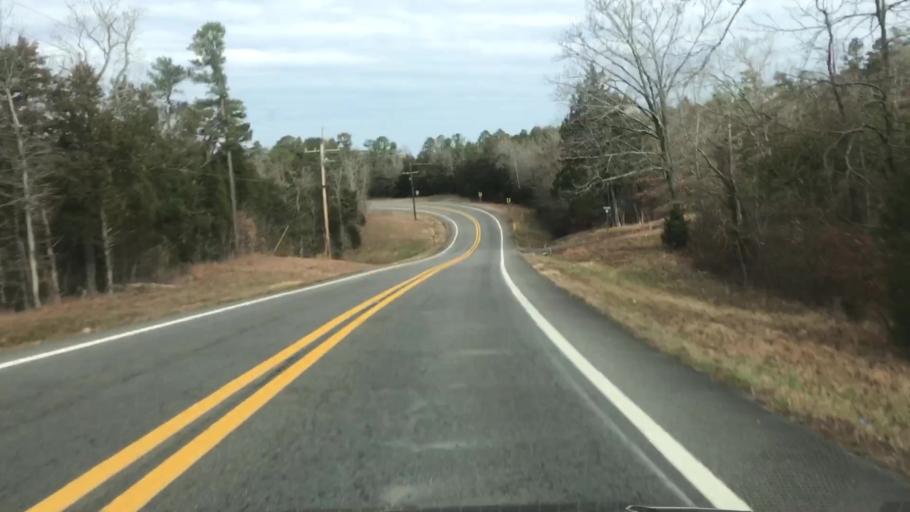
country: US
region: Arkansas
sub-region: Montgomery County
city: Mount Ida
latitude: 34.6174
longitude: -93.7037
